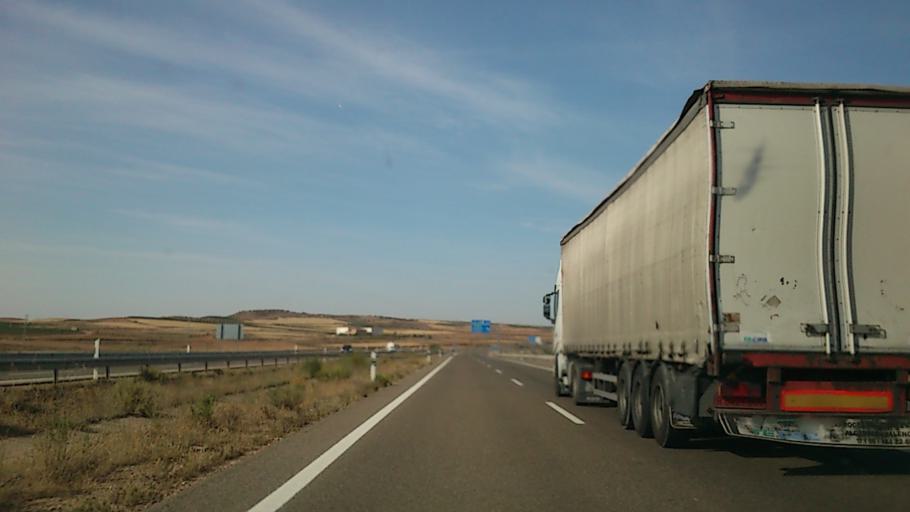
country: ES
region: Aragon
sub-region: Provincia de Zaragoza
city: Longares
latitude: 41.3980
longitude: -1.1801
